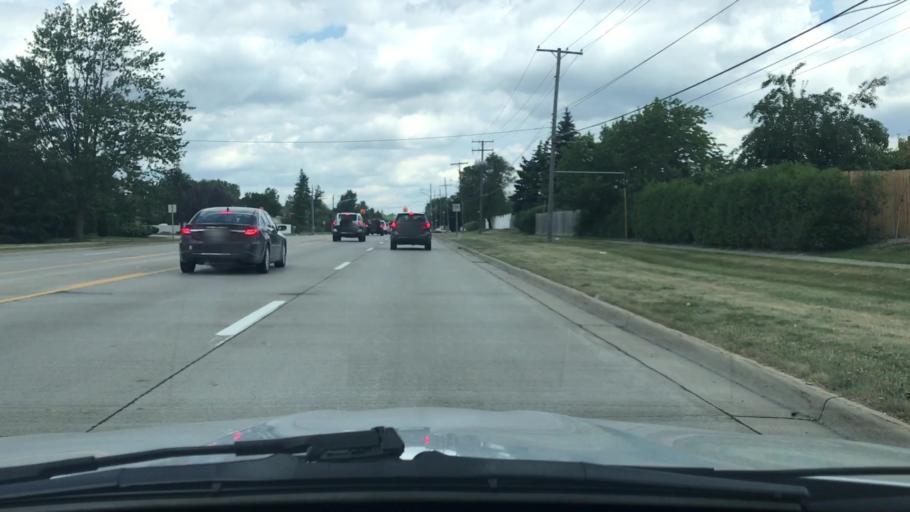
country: US
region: Michigan
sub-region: Macomb County
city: Sterling Heights
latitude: 42.5689
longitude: -83.0889
